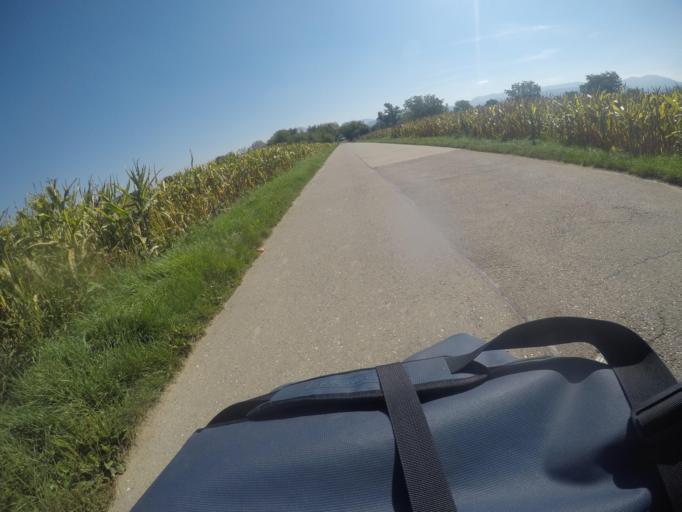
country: DE
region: Baden-Wuerttemberg
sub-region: Freiburg Region
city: Heitersheim
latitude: 47.8771
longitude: 7.6344
